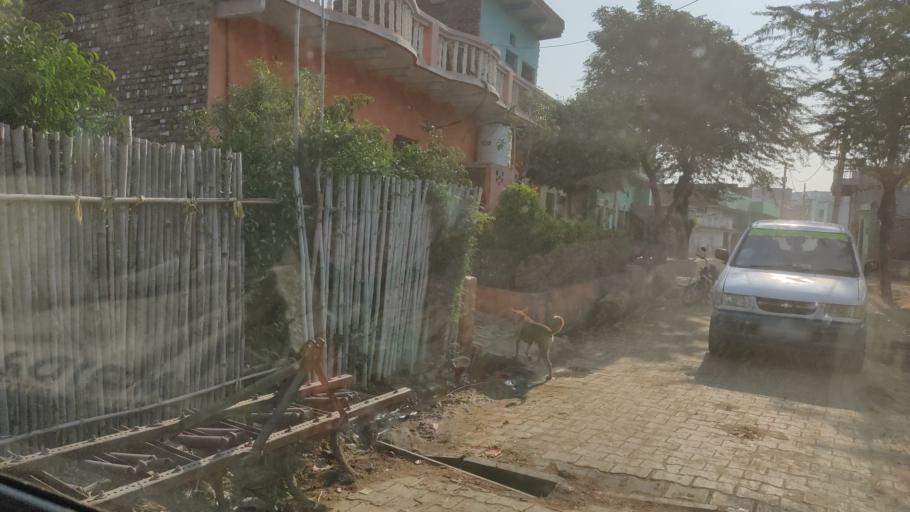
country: IN
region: Uttar Pradesh
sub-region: Mathura
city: Radha Kund
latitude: 27.5602
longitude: 77.5588
